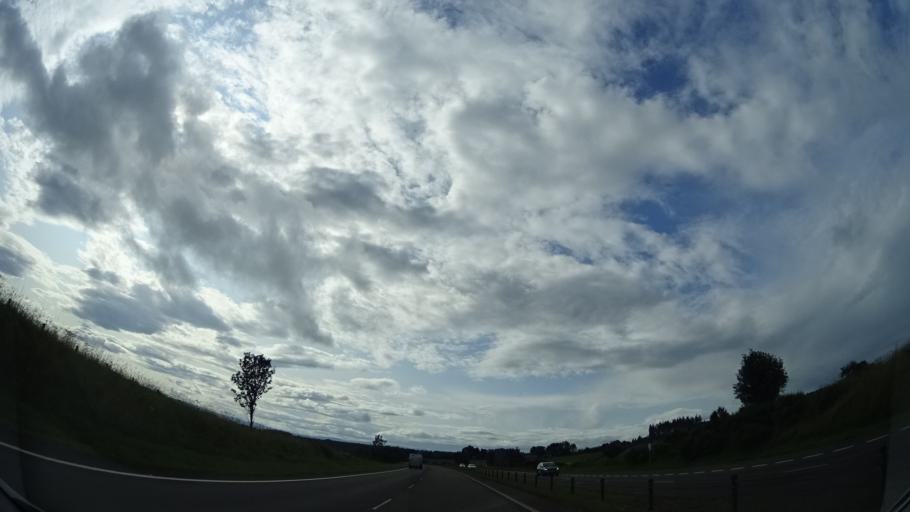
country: GB
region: Scotland
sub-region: Highland
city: Inverness
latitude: 57.5288
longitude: -4.3253
